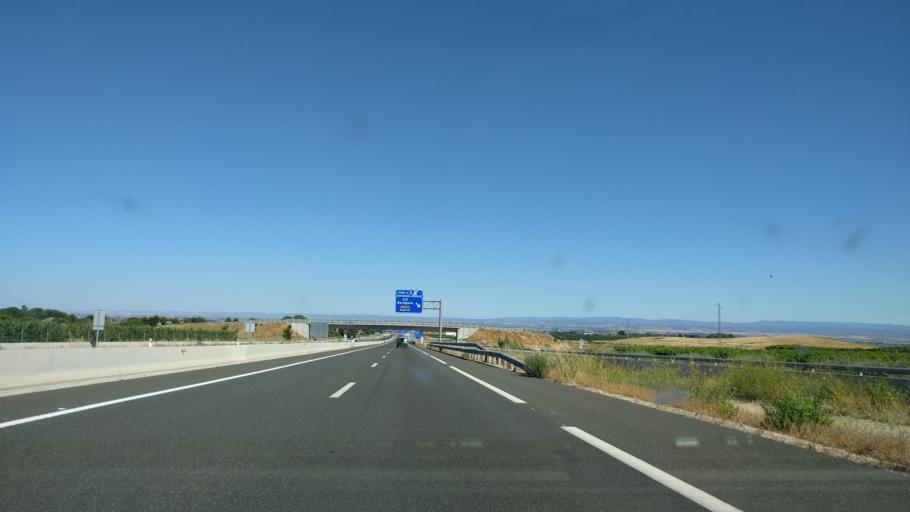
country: ES
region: Catalonia
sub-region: Provincia de Lleida
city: Alpicat
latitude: 41.6559
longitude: 0.5393
